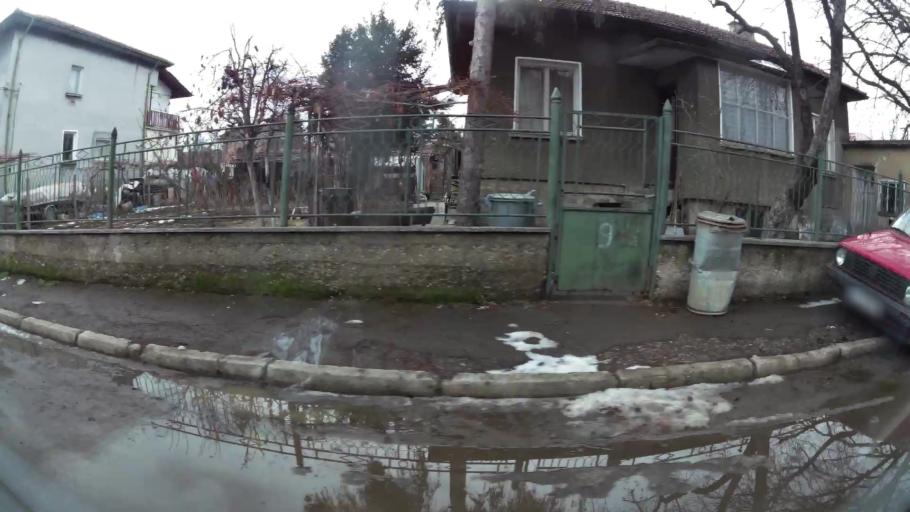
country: BG
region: Sofiya
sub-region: Obshtina Bozhurishte
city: Bozhurishte
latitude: 42.7441
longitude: 23.2616
